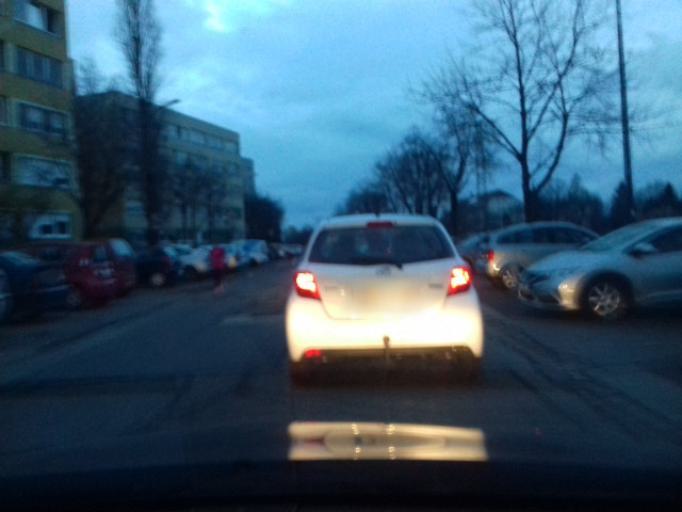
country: HU
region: Budapest
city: Budapest XVI. keruelet
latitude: 47.5074
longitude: 19.1528
